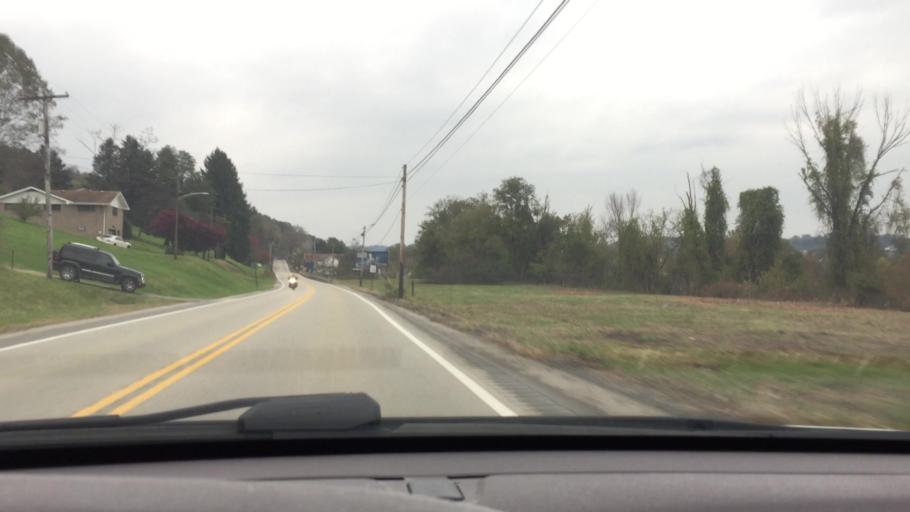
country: US
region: Pennsylvania
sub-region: Fayette County
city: Belle Vernon
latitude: 40.1141
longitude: -79.8593
